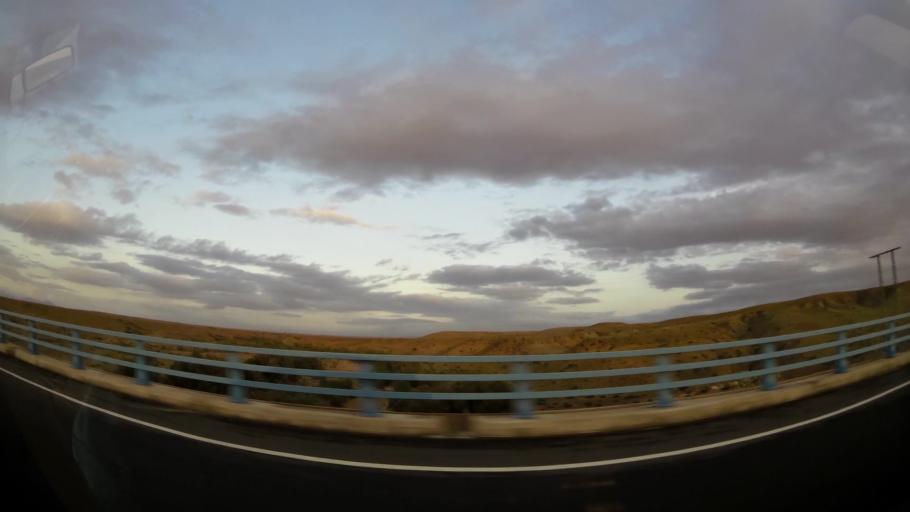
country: MA
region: Oriental
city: Taourirt
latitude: 34.5367
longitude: -2.9150
